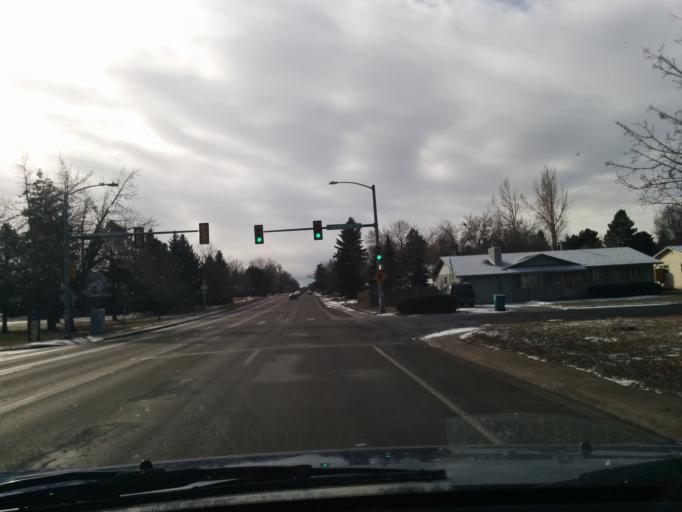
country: US
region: Colorado
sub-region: Larimer County
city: Fort Collins
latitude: 40.5718
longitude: -105.1152
